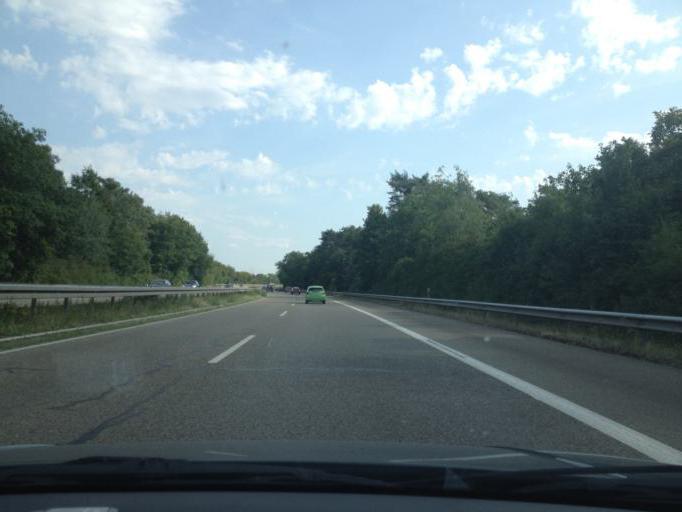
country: DE
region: Baden-Wuerttemberg
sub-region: Karlsruhe Region
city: Bruhl
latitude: 49.4278
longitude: 8.5372
